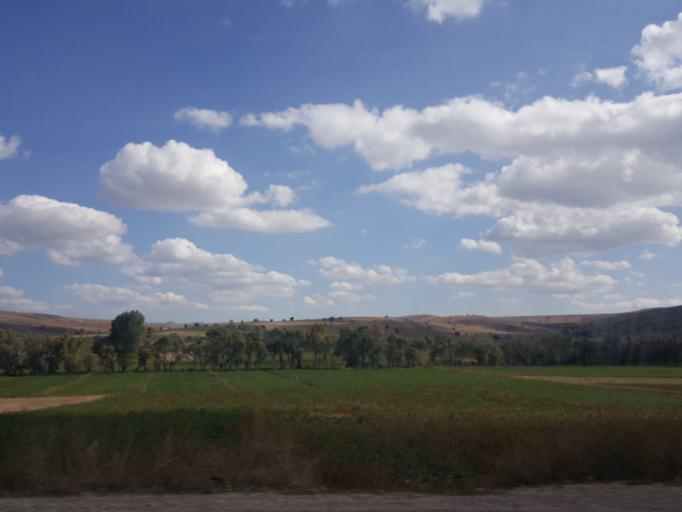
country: TR
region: Tokat
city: Camlibel
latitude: 40.1785
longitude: 36.4457
